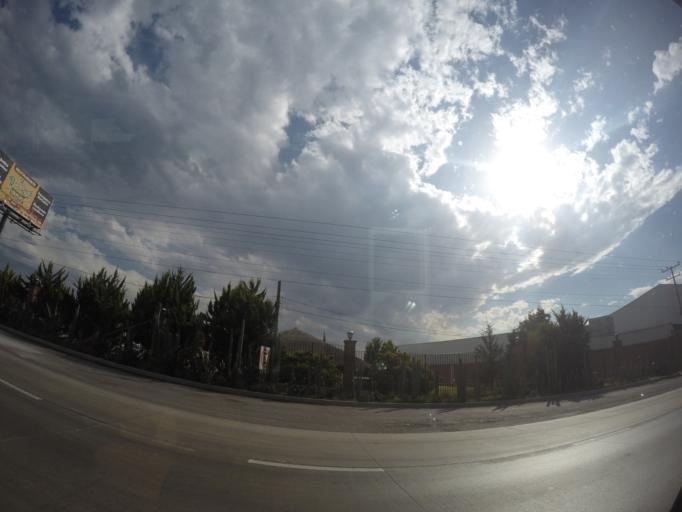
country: MX
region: Queretaro
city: El Sauz
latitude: 20.4870
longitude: -100.1202
